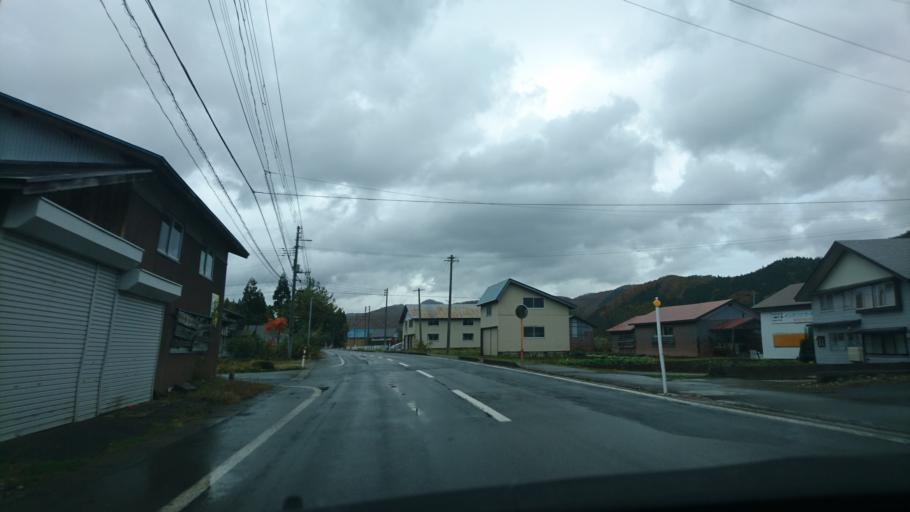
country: JP
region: Akita
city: Kakunodatemachi
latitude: 39.4889
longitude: 140.8085
